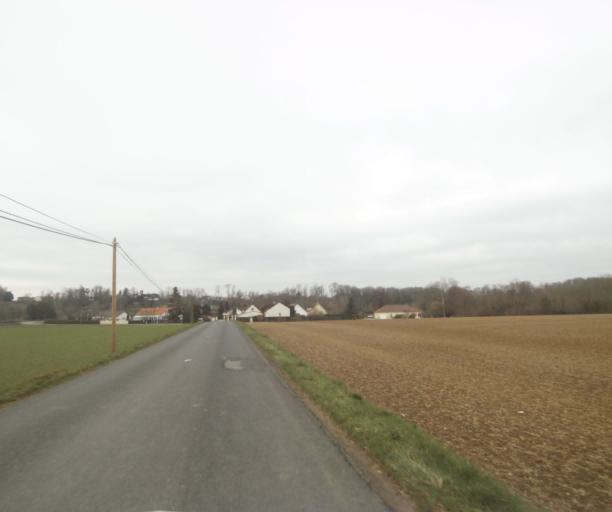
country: FR
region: Champagne-Ardenne
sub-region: Departement de la Haute-Marne
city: Villiers-en-Lieu
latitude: 48.6340
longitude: 4.8617
